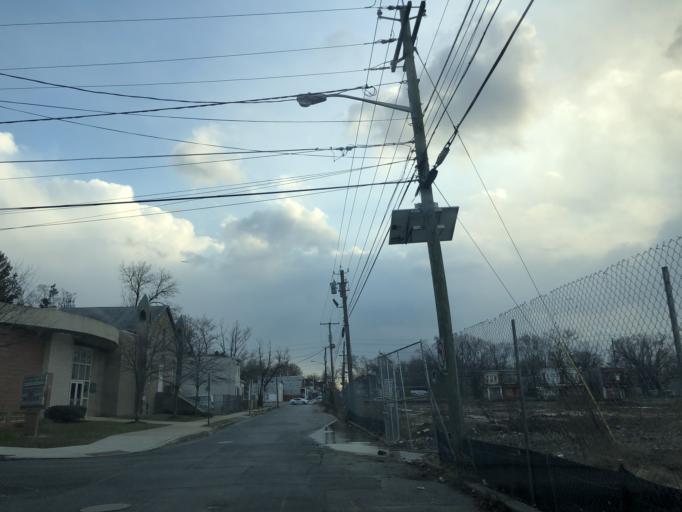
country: US
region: New Jersey
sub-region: Camden County
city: Camden
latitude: 39.9209
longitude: -75.1087
